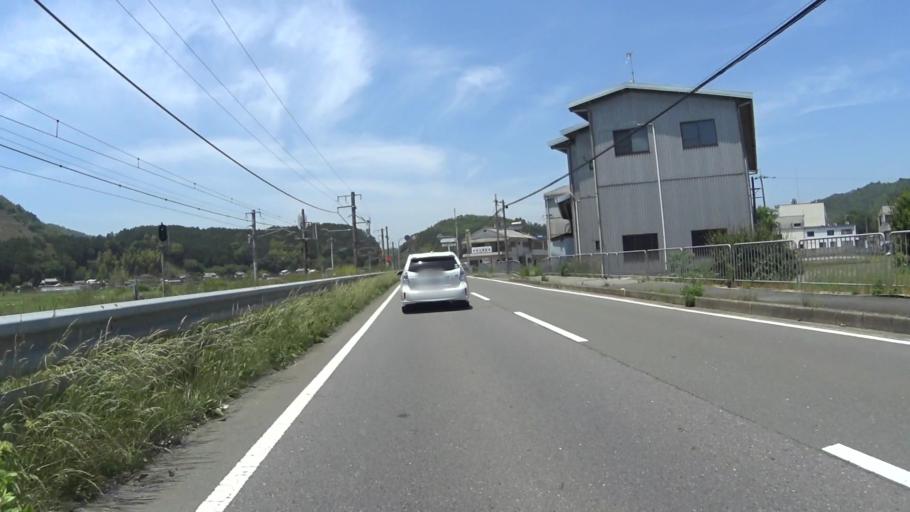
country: JP
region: Kyoto
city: Kameoka
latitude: 35.0772
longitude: 135.5210
